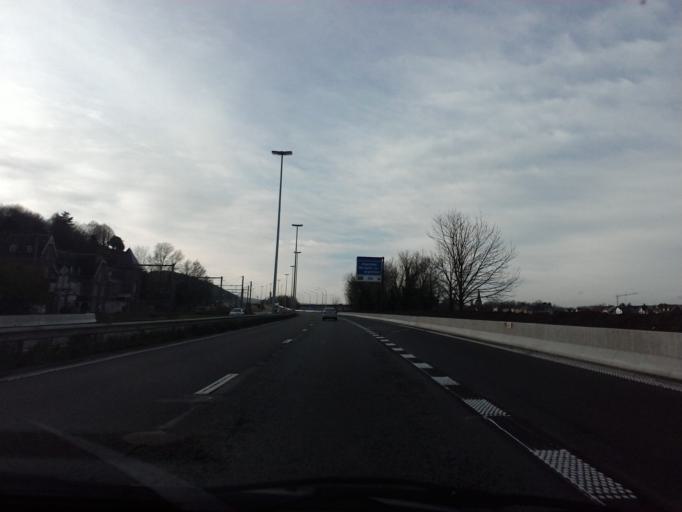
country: BE
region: Wallonia
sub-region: Province de Liege
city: Vise
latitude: 50.7150
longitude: 5.6871
